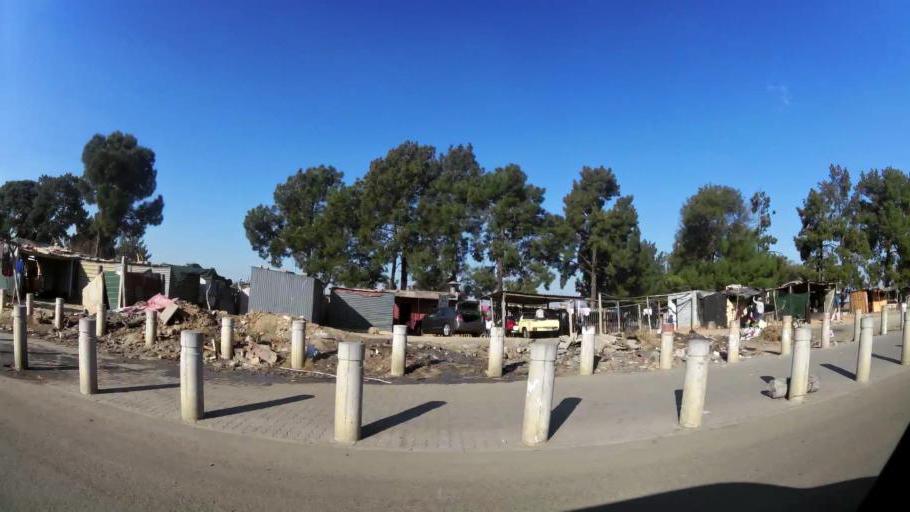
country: ZA
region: Gauteng
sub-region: West Rand District Municipality
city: Muldersdriseloop
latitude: -26.0547
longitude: 27.9044
